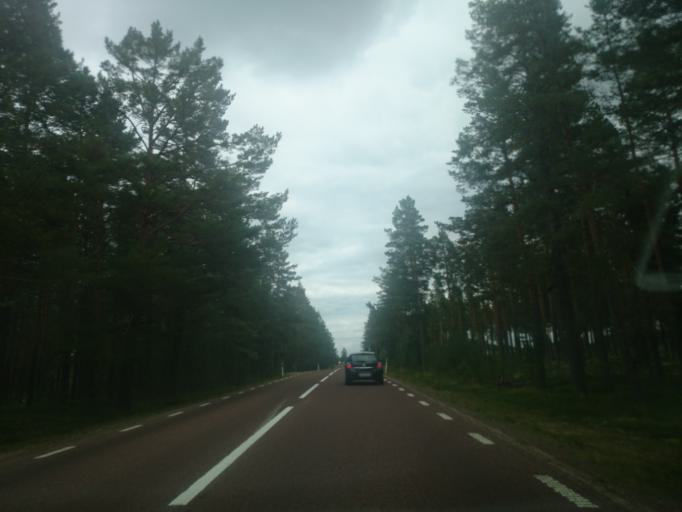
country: SE
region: Jaemtland
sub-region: Harjedalens Kommun
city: Sveg
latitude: 62.0386
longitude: 14.4451
